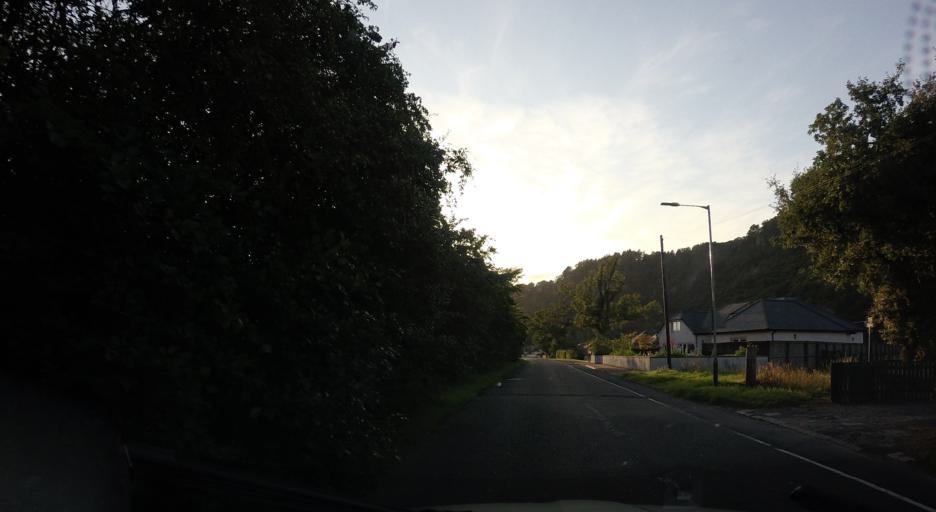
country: GB
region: Scotland
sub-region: Perth and Kinross
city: Scone
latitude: 56.3839
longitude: -3.3957
